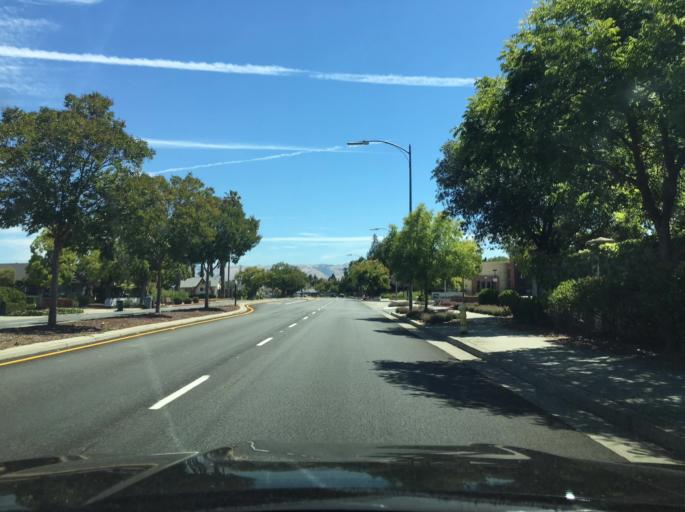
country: US
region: California
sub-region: Santa Clara County
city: Cambrian Park
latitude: 37.2402
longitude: -121.8935
